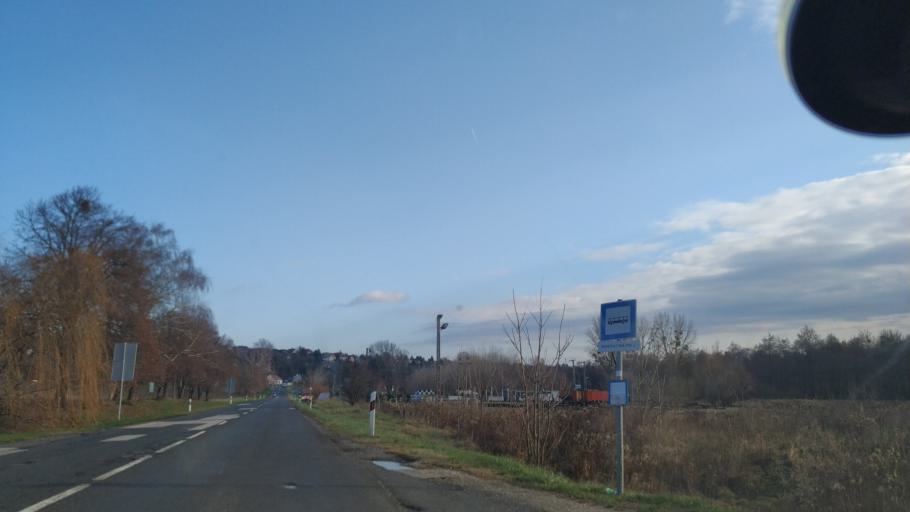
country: HU
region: Zala
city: Cserszegtomaj
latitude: 46.7929
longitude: 17.2053
